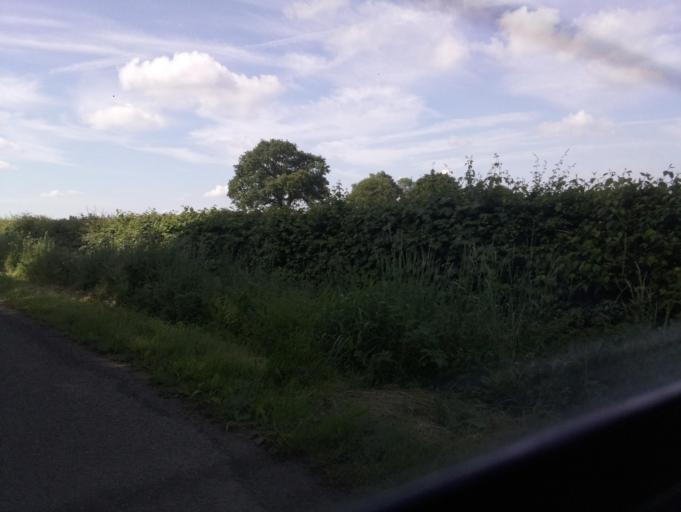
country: GB
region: England
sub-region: Lincolnshire
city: Skellingthorpe
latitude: 53.1390
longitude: -0.6333
